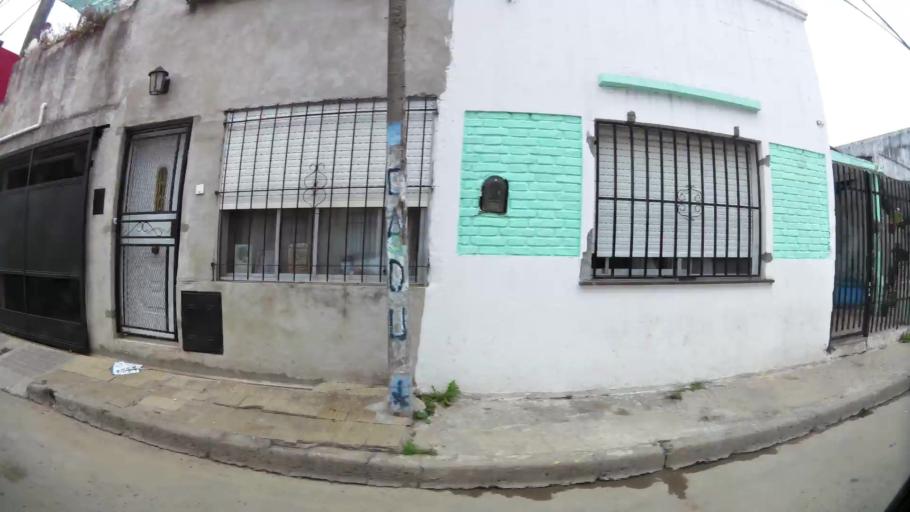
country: AR
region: Buenos Aires
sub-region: Partido de Zarate
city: Zarate
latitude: -34.1080
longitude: -59.0205
